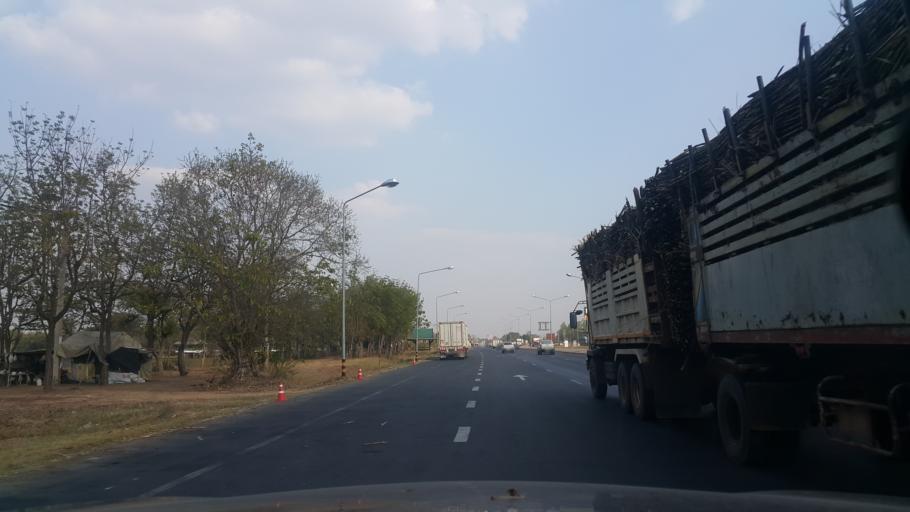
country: TH
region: Buriram
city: Nang Rong
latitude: 14.6323
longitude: 102.8283
